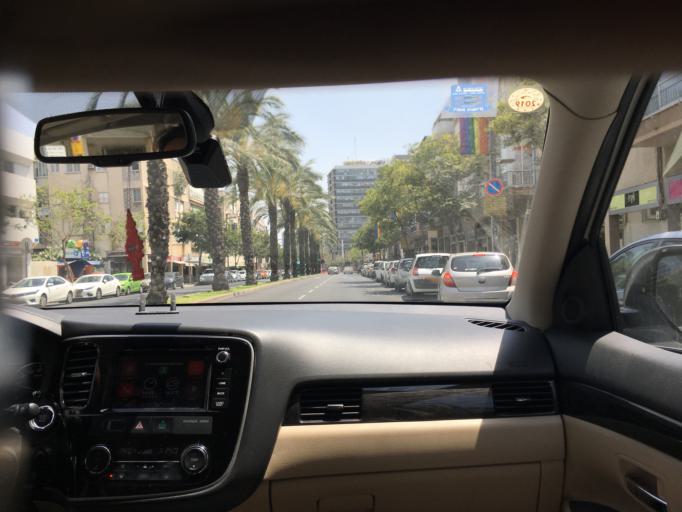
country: IL
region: Tel Aviv
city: Tel Aviv
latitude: 32.0844
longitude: 34.7816
